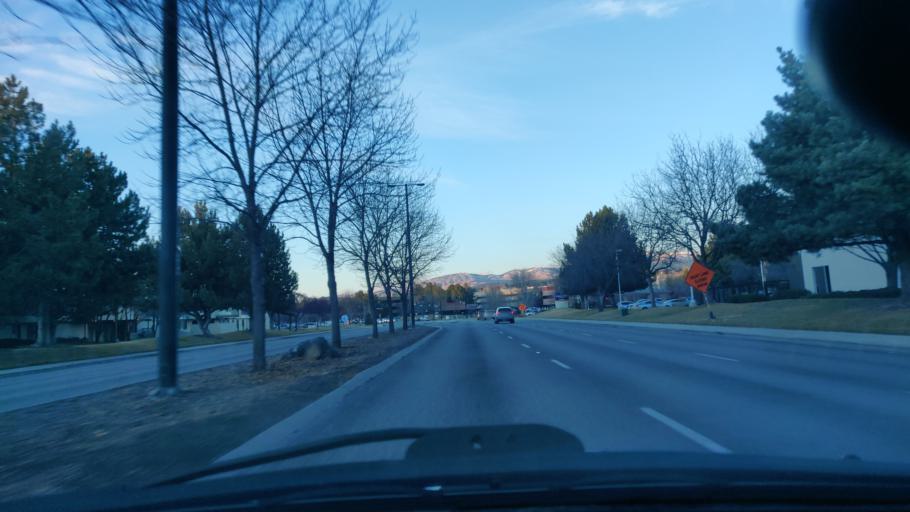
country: US
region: Idaho
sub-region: Ada County
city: Boise
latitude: 43.5943
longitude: -116.1779
